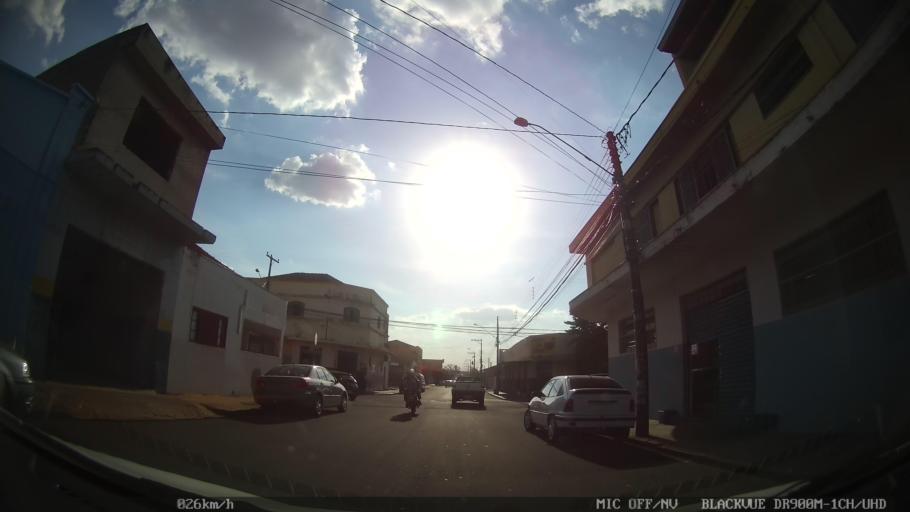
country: BR
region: Sao Paulo
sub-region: Ribeirao Preto
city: Ribeirao Preto
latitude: -21.1643
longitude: -47.8066
